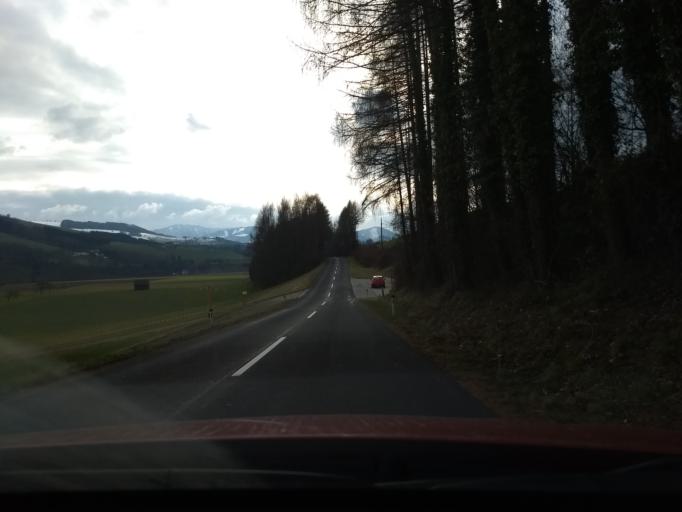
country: AT
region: Upper Austria
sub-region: Politischer Bezirk Steyr-Land
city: Garsten
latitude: 47.9997
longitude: 14.3936
